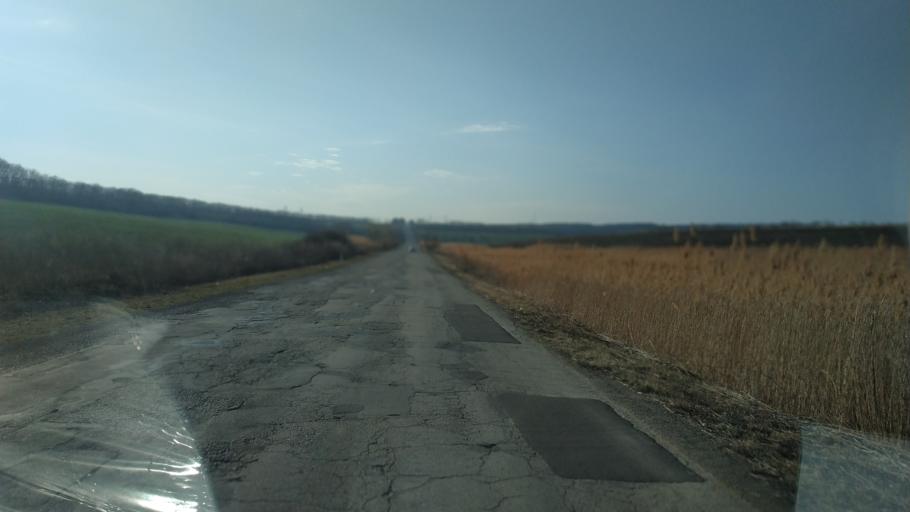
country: MD
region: Chisinau
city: Singera
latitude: 46.8847
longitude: 29.0393
